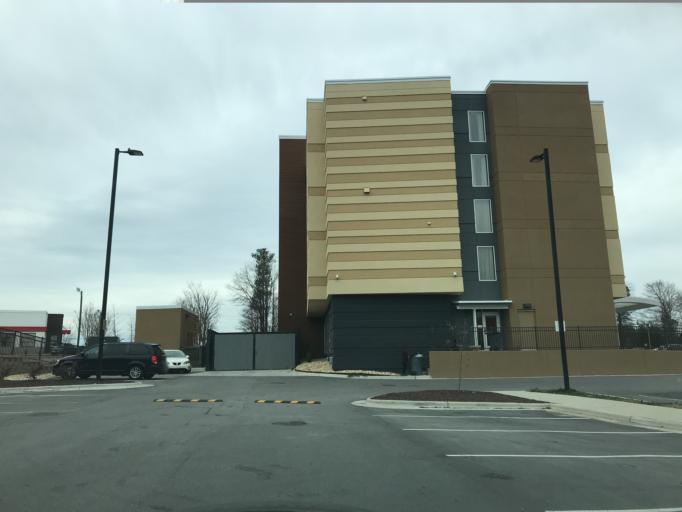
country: US
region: North Carolina
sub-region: Wake County
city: Raleigh
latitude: 35.8713
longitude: -78.5781
